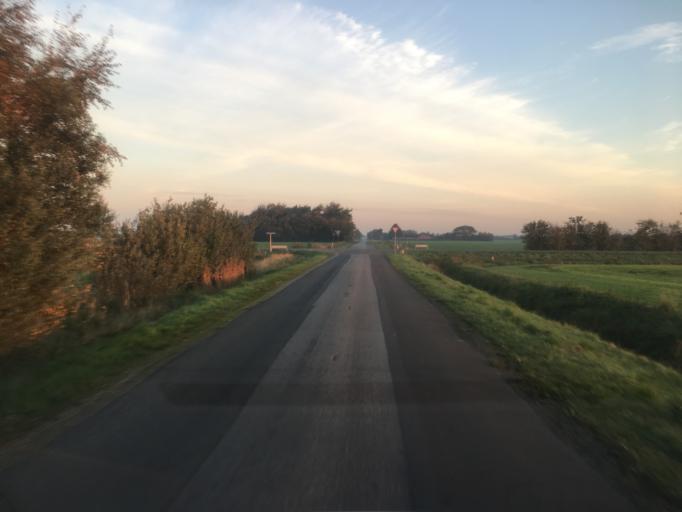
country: DK
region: South Denmark
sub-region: Tonder Kommune
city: Logumkloster
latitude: 55.0621
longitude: 9.0233
